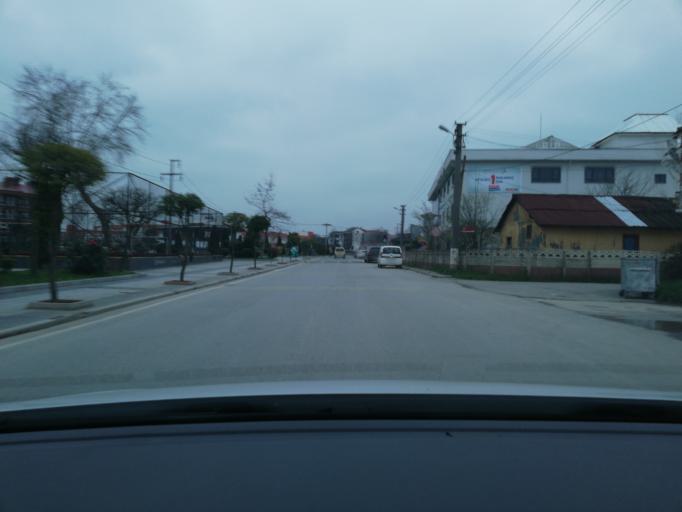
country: TR
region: Duzce
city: Duzce
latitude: 40.8368
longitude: 31.1527
